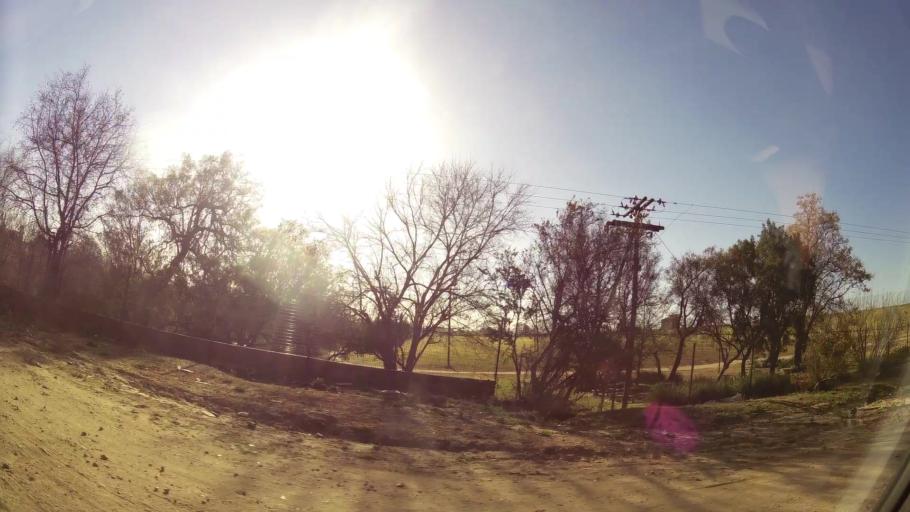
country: ZA
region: Gauteng
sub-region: City of Johannesburg Metropolitan Municipality
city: Diepsloot
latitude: -25.9530
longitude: 27.9622
